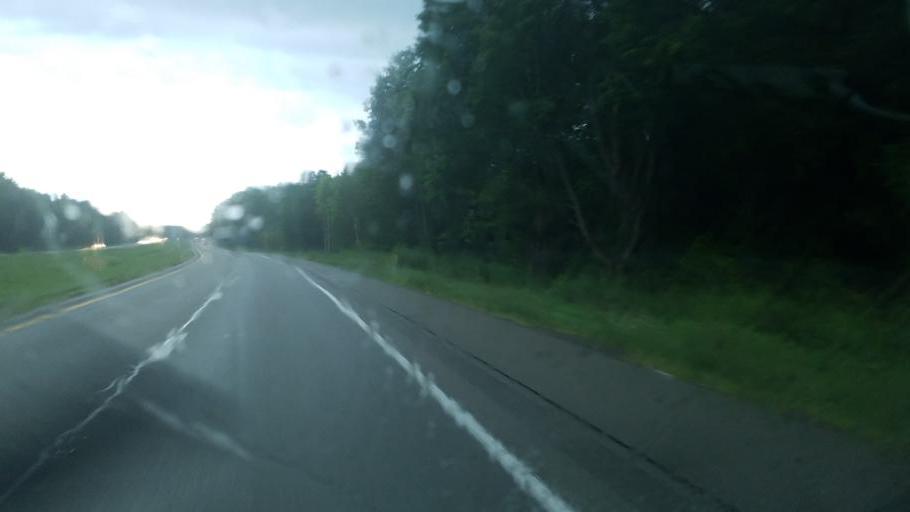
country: US
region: Pennsylvania
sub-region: Mercer County
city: Grove City
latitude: 41.1276
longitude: -80.1528
